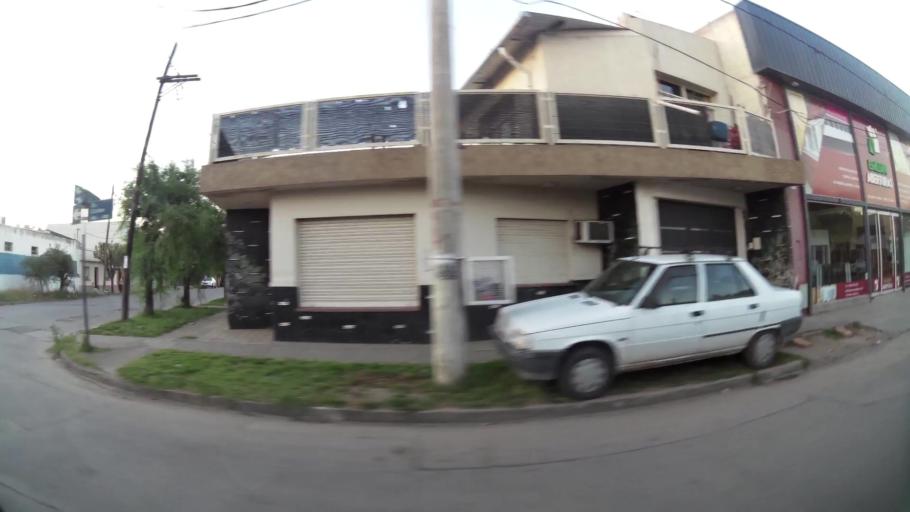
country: AR
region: Cordoba
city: Villa Maria
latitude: -32.4096
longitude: -63.2581
